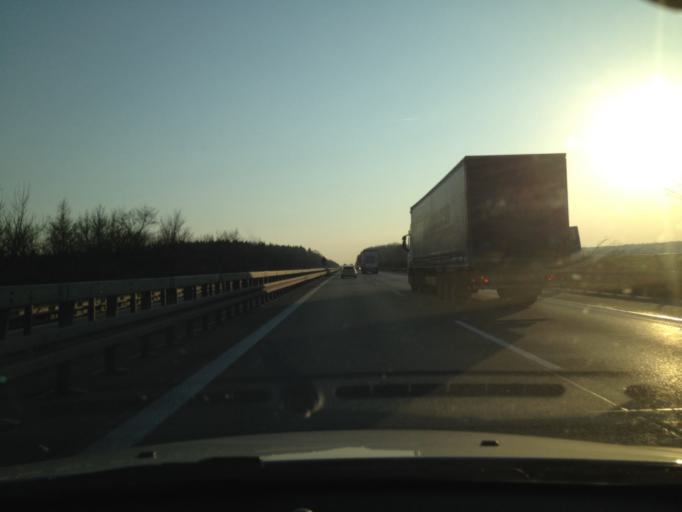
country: DE
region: Baden-Wuerttemberg
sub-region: Tuebingen Region
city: Setzingen
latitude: 48.5690
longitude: 10.1500
